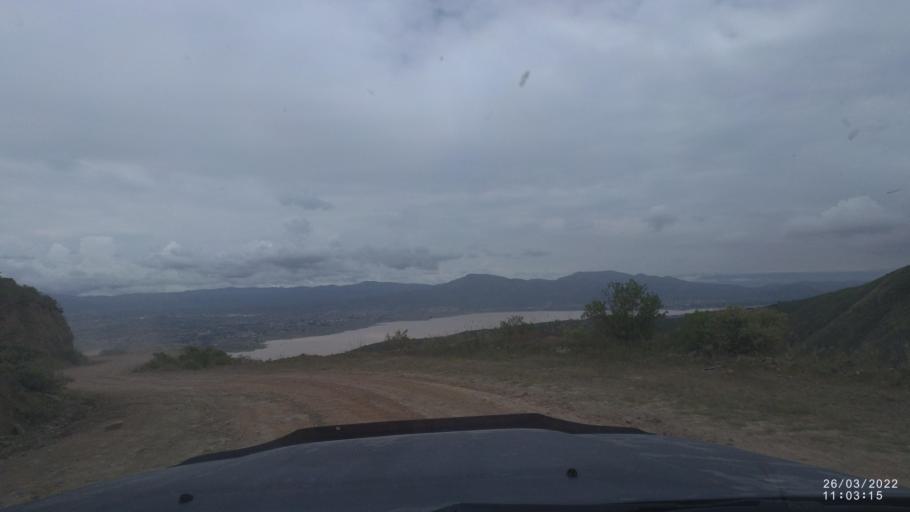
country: BO
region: Cochabamba
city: Tarata
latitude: -17.5258
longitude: -66.0255
